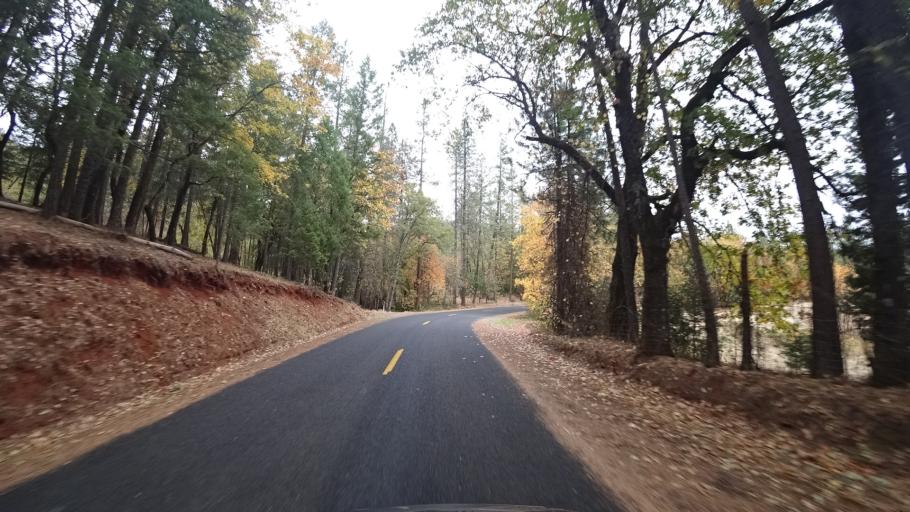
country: US
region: California
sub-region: Siskiyou County
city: Happy Camp
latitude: 41.8496
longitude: -123.1810
